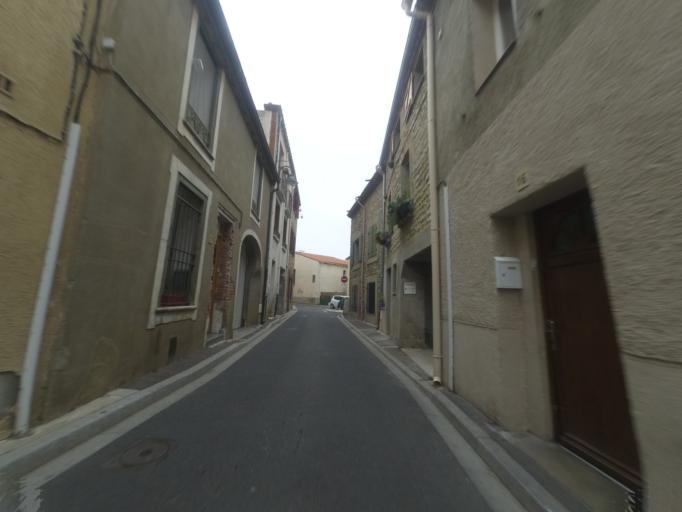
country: FR
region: Languedoc-Roussillon
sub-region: Departement des Pyrenees-Orientales
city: Villeneuve-la-Riviere
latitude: 42.6932
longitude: 2.8030
